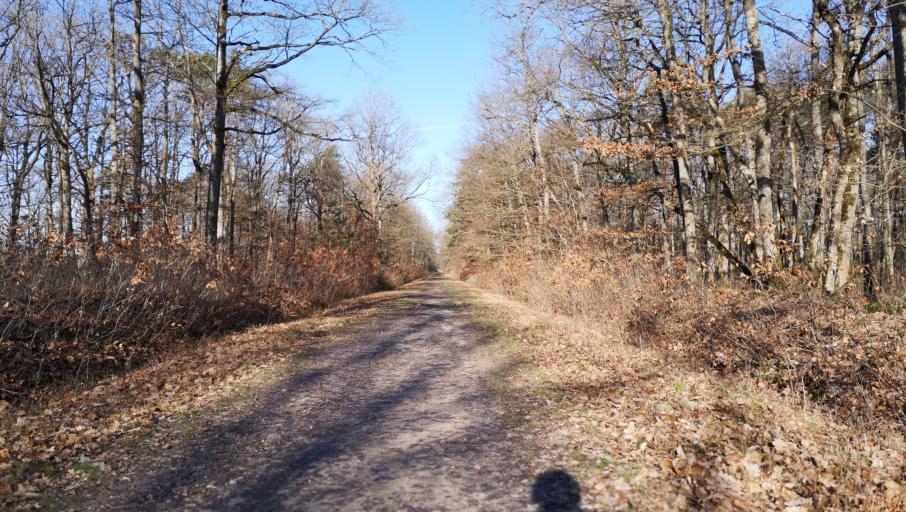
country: FR
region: Centre
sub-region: Departement du Loiret
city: Chanteau
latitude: 47.9527
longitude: 1.9694
